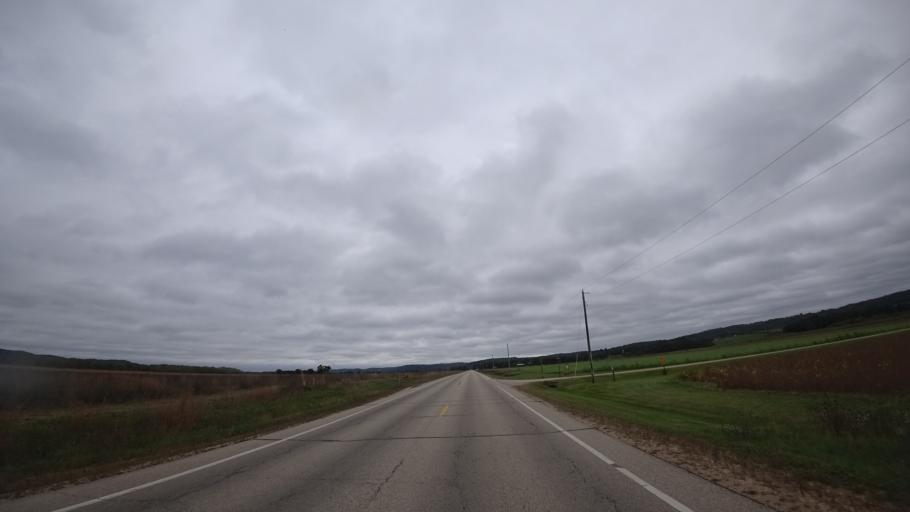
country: US
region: Wisconsin
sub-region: Grant County
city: Boscobel
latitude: 43.2053
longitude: -90.5894
